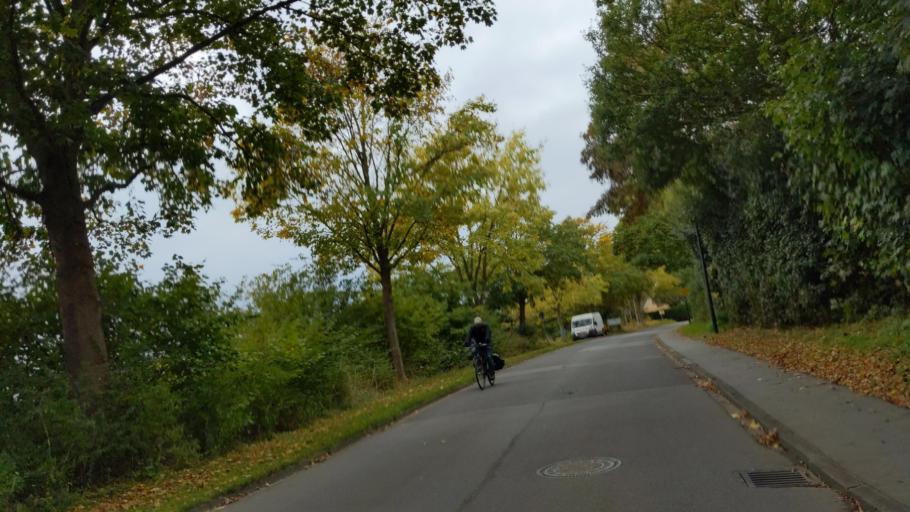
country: DE
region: Schleswig-Holstein
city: Scharbeutz
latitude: 54.0450
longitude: 10.7354
